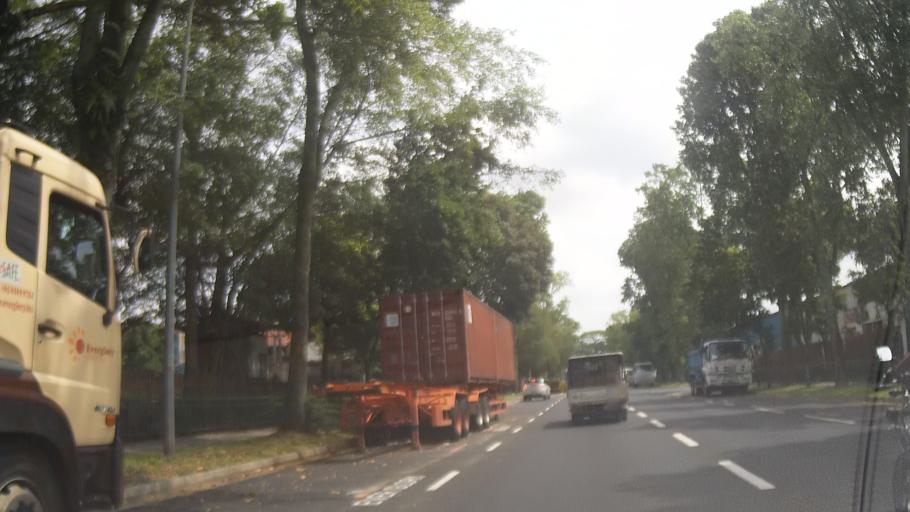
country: MY
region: Johor
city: Johor Bahru
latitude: 1.4170
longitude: 103.7488
